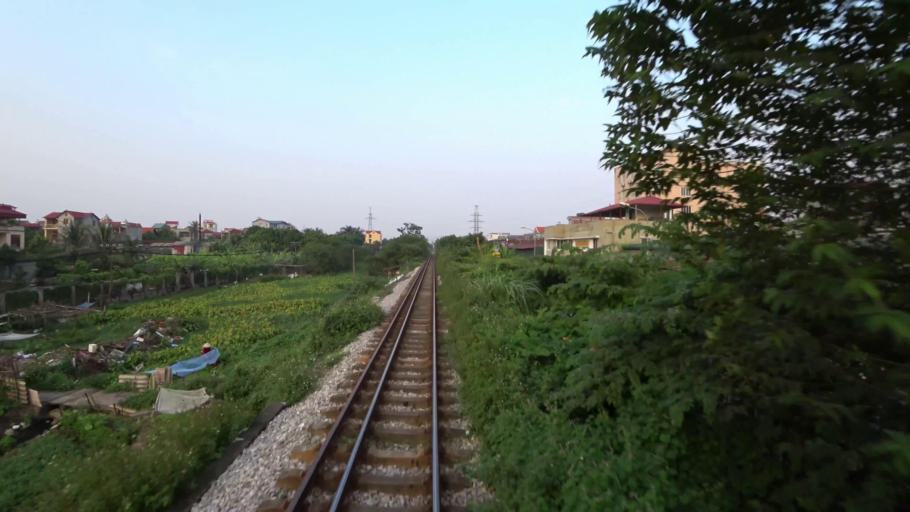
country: VN
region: Ha Noi
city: Trau Quy
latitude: 21.0873
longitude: 105.9178
